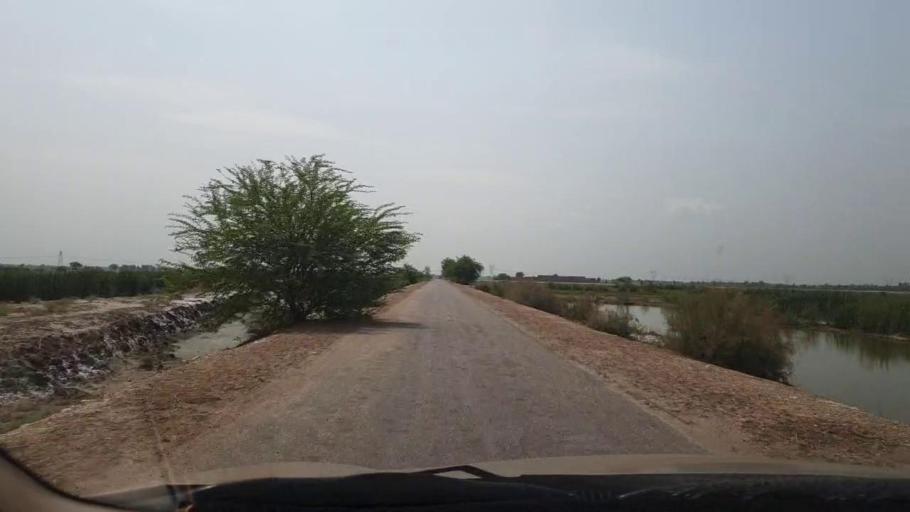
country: PK
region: Sindh
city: Goth Garelo
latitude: 27.4999
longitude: 68.1160
